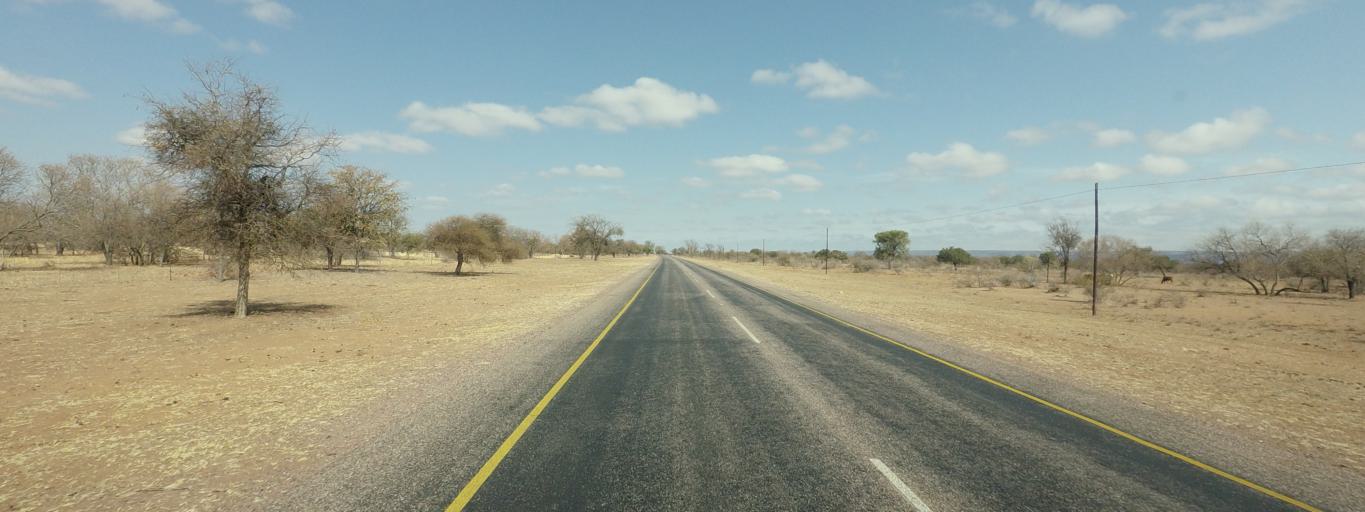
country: BW
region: Central
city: Ramokgonami
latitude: -22.7944
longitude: 27.4657
